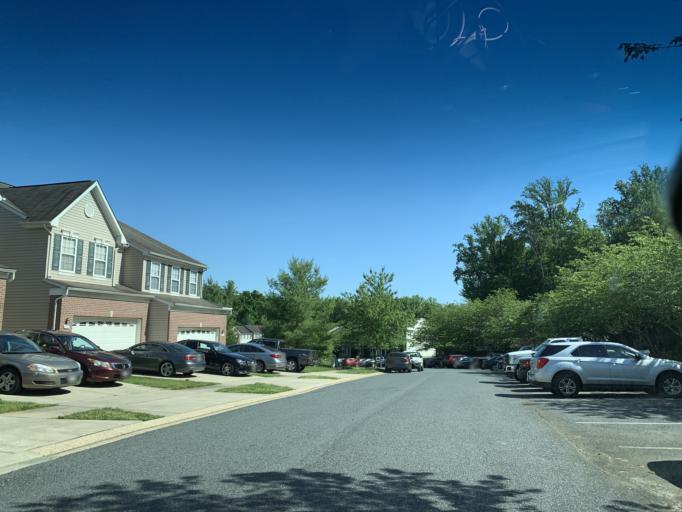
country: US
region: Maryland
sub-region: Harford County
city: Riverside
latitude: 39.4932
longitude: -76.2254
